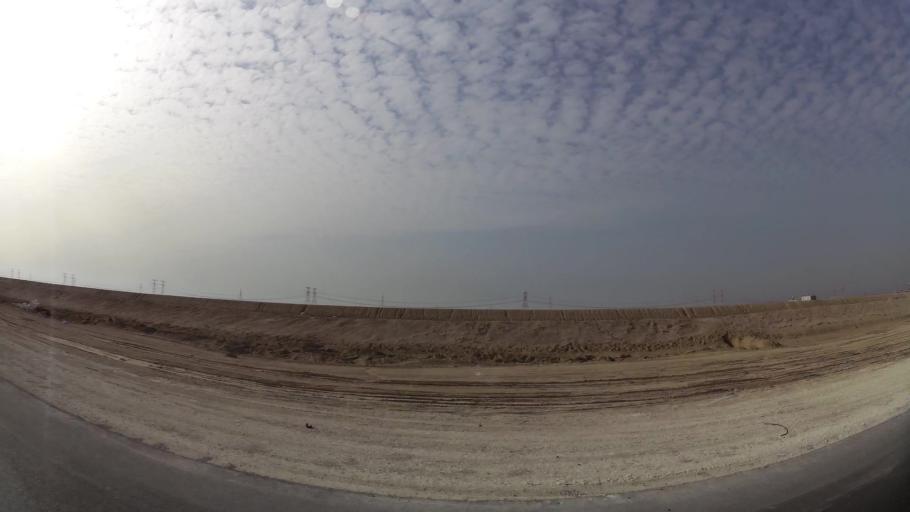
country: AE
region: Abu Dhabi
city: Abu Dhabi
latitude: 24.2516
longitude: 54.4776
